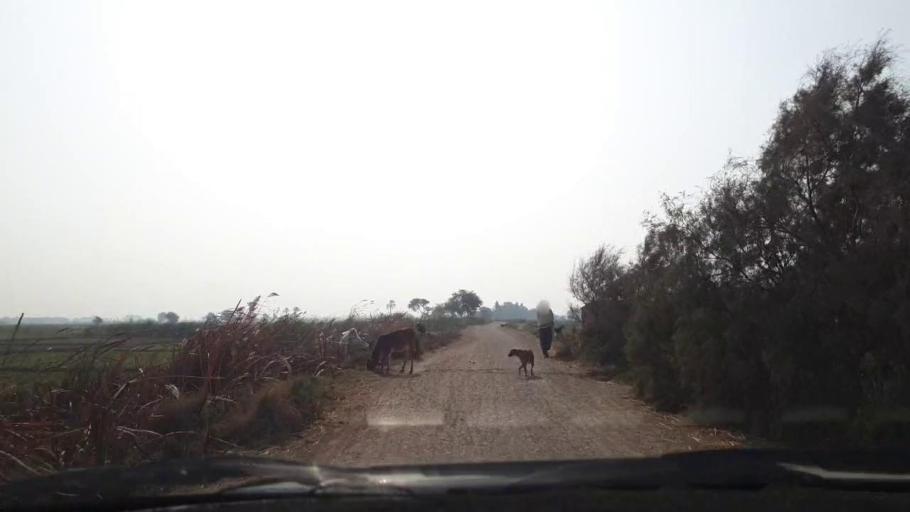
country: PK
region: Sindh
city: Tando Muhammad Khan
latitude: 25.0158
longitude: 68.4511
